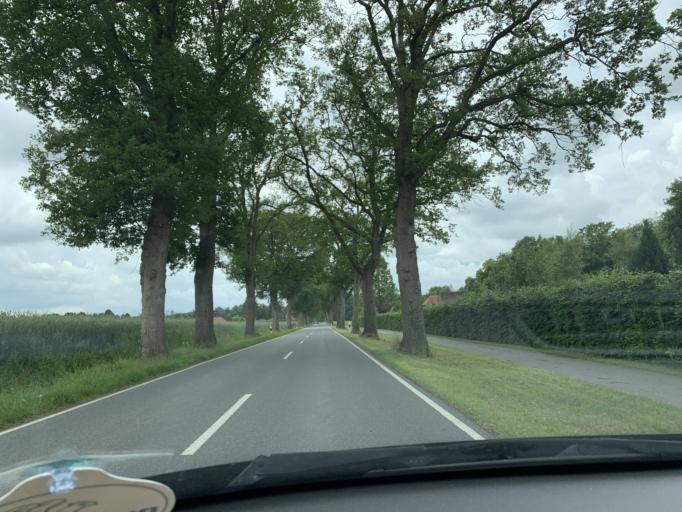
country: DE
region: Lower Saxony
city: Westerstede
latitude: 53.2896
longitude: 7.9873
